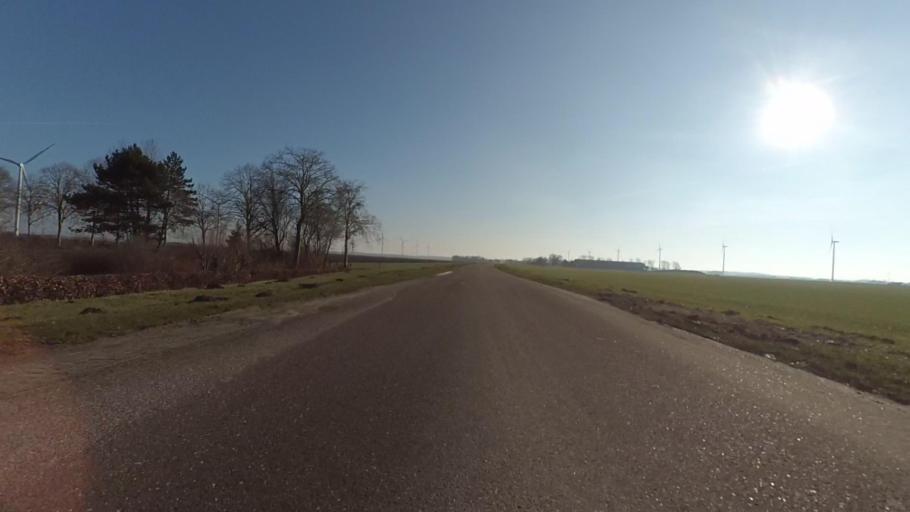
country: NL
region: Utrecht
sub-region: Gemeente Bunschoten
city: Spakenburg
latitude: 52.3005
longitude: 5.3838
